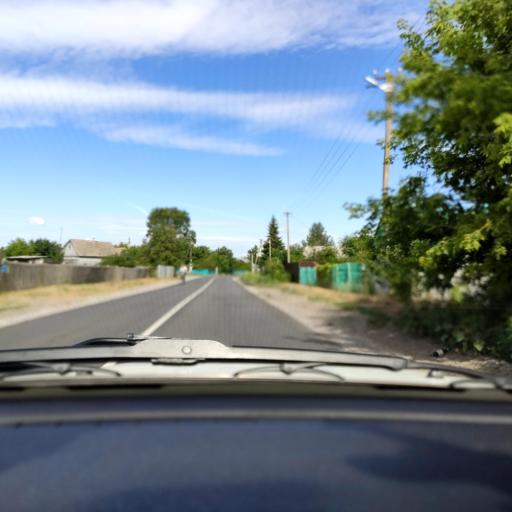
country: RU
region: Voronezj
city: Uglyanets
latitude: 51.8604
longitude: 39.6730
